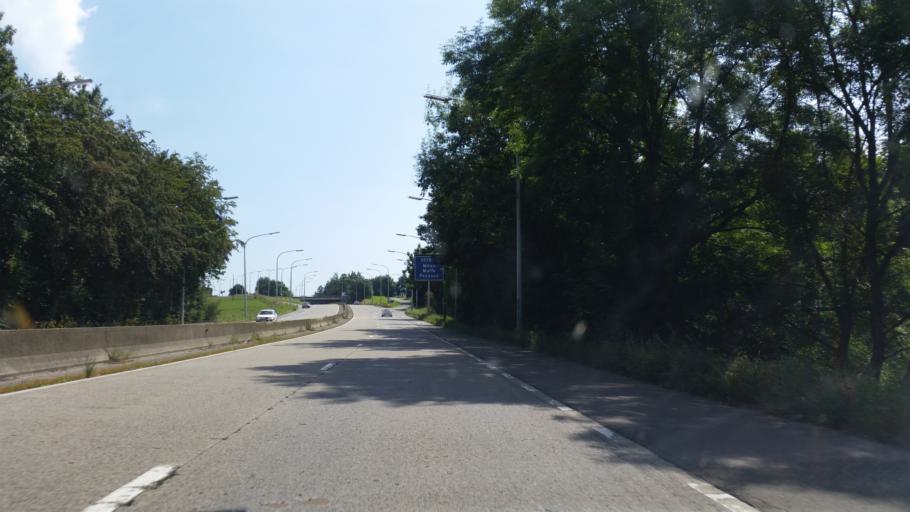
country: BE
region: Wallonia
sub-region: Province de Namur
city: Hamois
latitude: 50.2879
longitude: 5.1785
